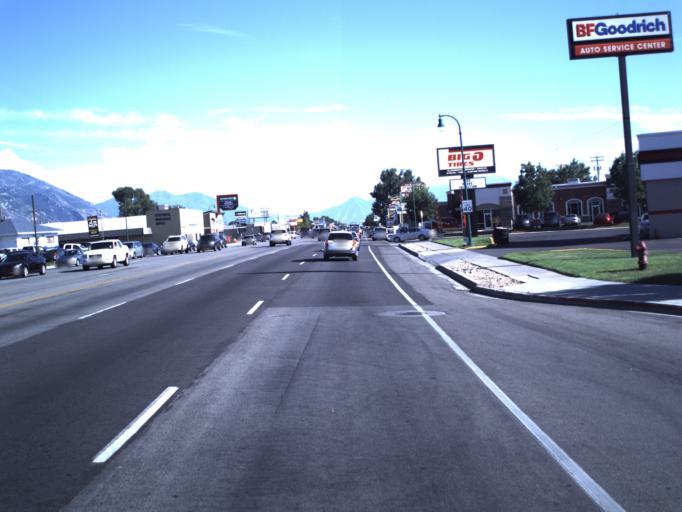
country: US
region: Utah
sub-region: Utah County
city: Orem
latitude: 40.3109
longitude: -111.7012
